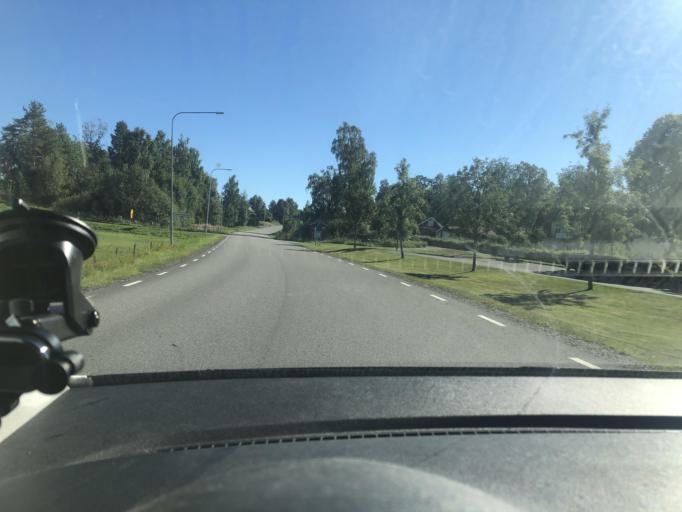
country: SE
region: Joenkoeping
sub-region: Jonkopings Kommun
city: Huskvarna
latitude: 57.7957
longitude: 14.3130
